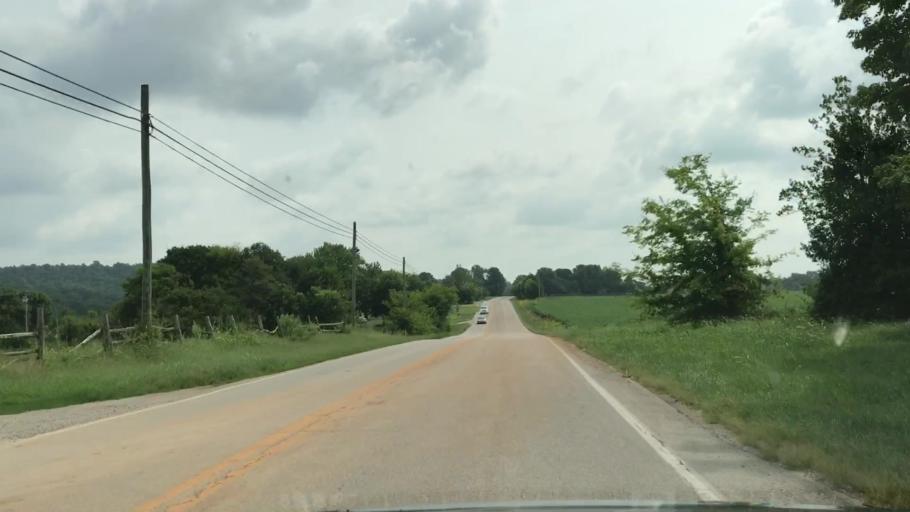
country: US
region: Kentucky
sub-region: Barren County
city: Cave City
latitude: 37.0922
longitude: -86.0929
